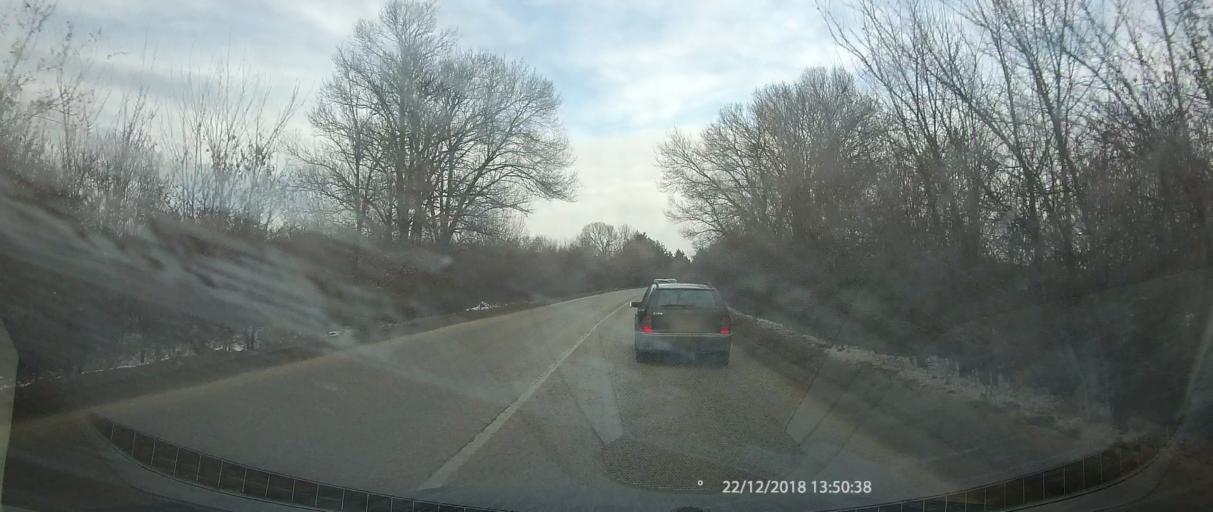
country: BG
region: Lovech
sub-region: Obshtina Lukovit
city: Lukovit
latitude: 43.2803
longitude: 24.2027
